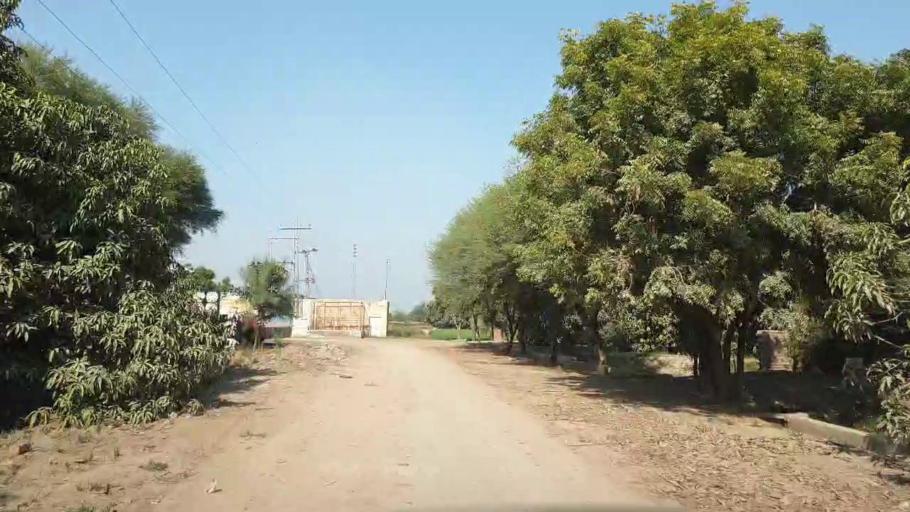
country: PK
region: Sindh
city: Tando Allahyar
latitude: 25.5596
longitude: 68.7092
